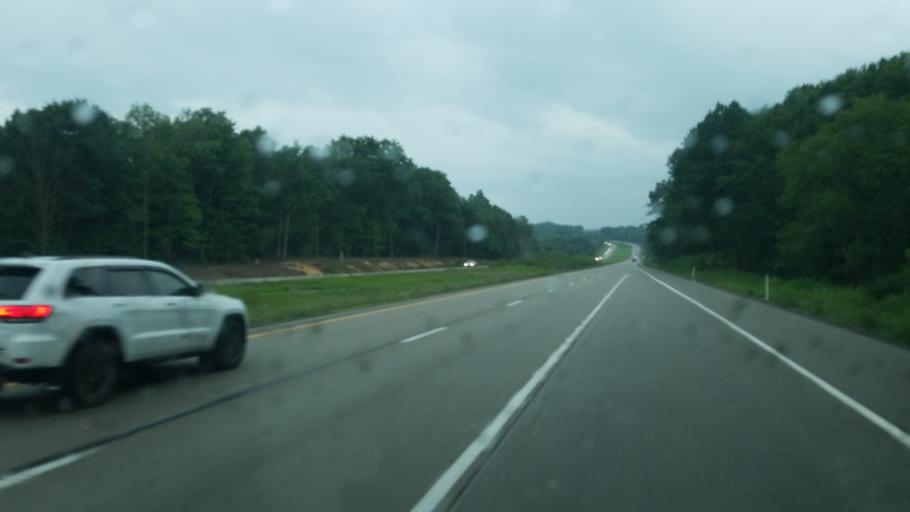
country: US
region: Pennsylvania
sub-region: Mercer County
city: Grove City
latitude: 41.1928
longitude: -80.1624
